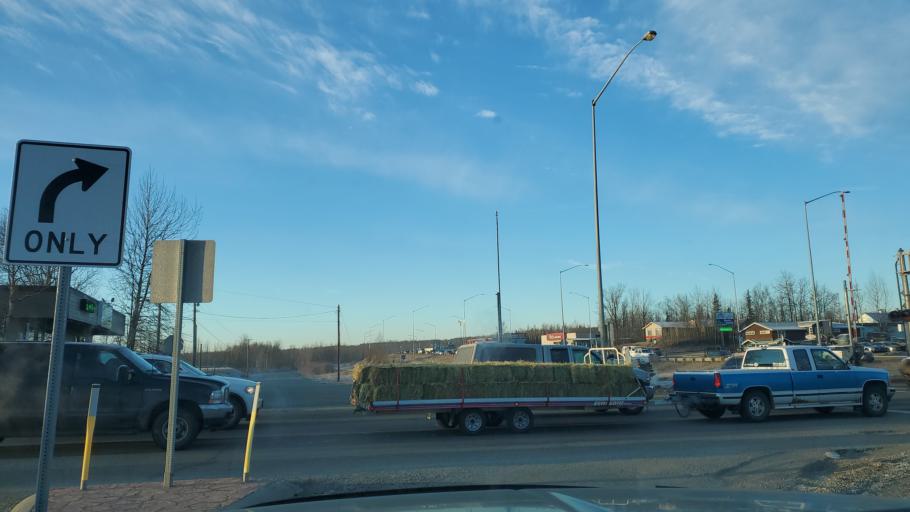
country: US
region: Alaska
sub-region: Matanuska-Susitna Borough
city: Wasilla
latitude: 61.5803
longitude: -149.4412
